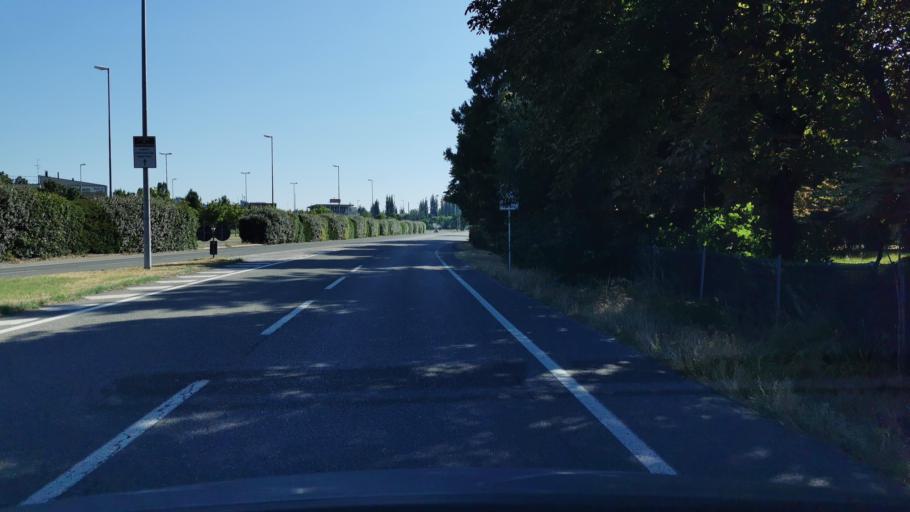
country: IT
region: Emilia-Romagna
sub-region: Provincia di Modena
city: Santa Croce Scuole
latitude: 44.7731
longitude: 10.8577
